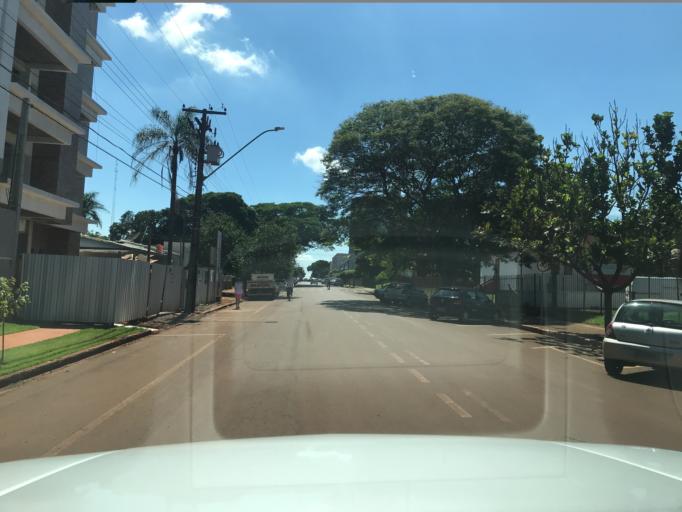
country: BR
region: Parana
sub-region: Palotina
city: Palotina
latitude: -24.2861
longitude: -53.8425
